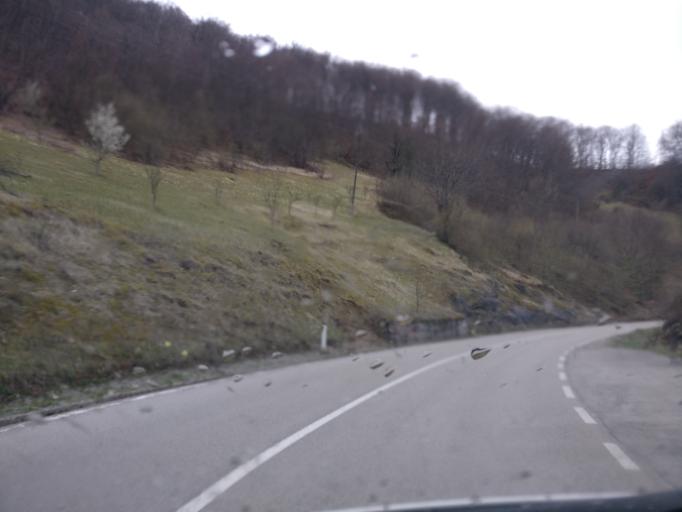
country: ME
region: Opstina Pluzine
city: Pluzine
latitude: 43.1461
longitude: 18.8337
